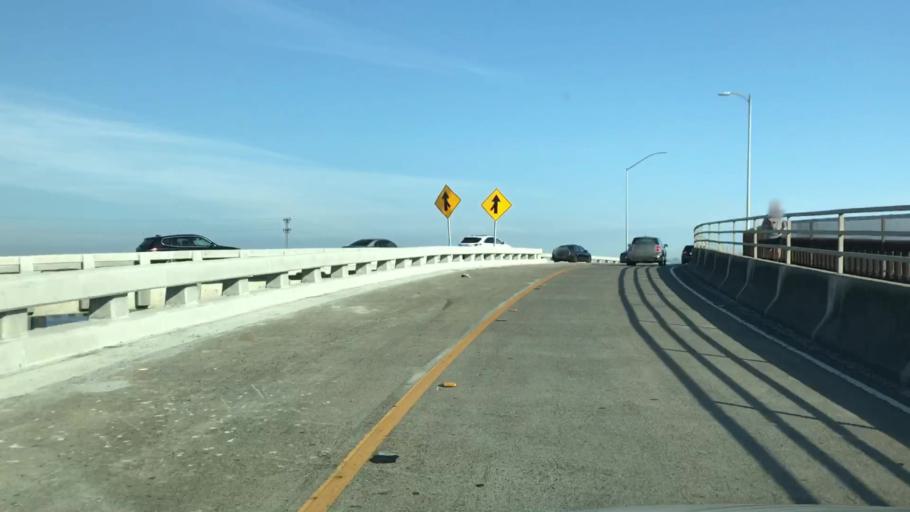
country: US
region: California
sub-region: Marin County
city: Larkspur
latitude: 37.9439
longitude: -122.5168
